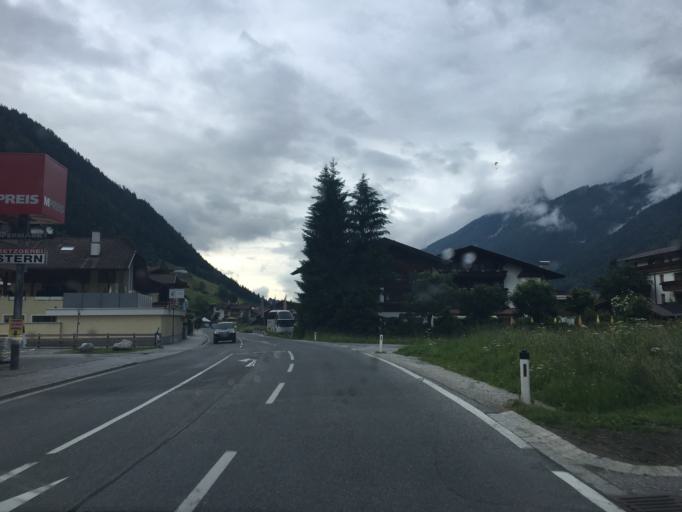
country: AT
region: Tyrol
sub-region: Politischer Bezirk Innsbruck Land
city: Neustift im Stubaital
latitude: 47.1119
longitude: 11.3098
